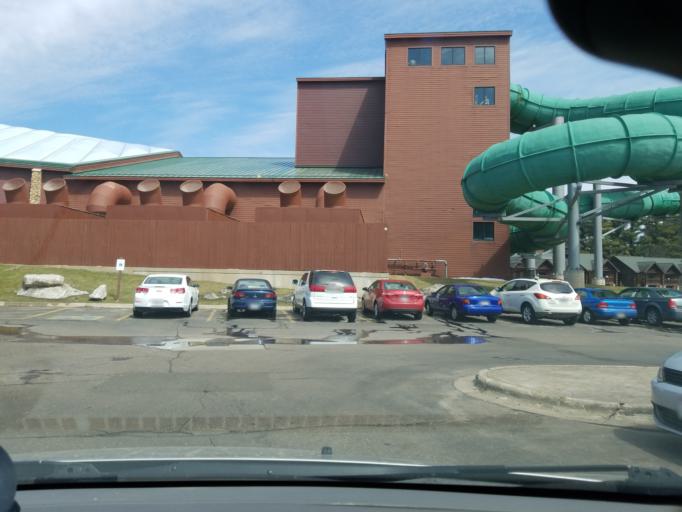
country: US
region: Wisconsin
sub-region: Sauk County
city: Lake Delton
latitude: 43.5861
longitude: -89.7821
